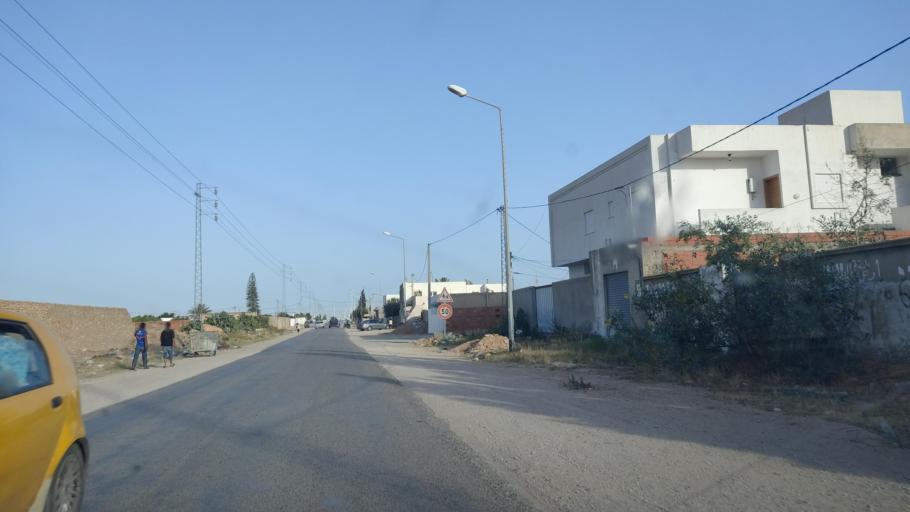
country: TN
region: Safaqis
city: Sfax
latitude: 34.7997
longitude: 10.6750
